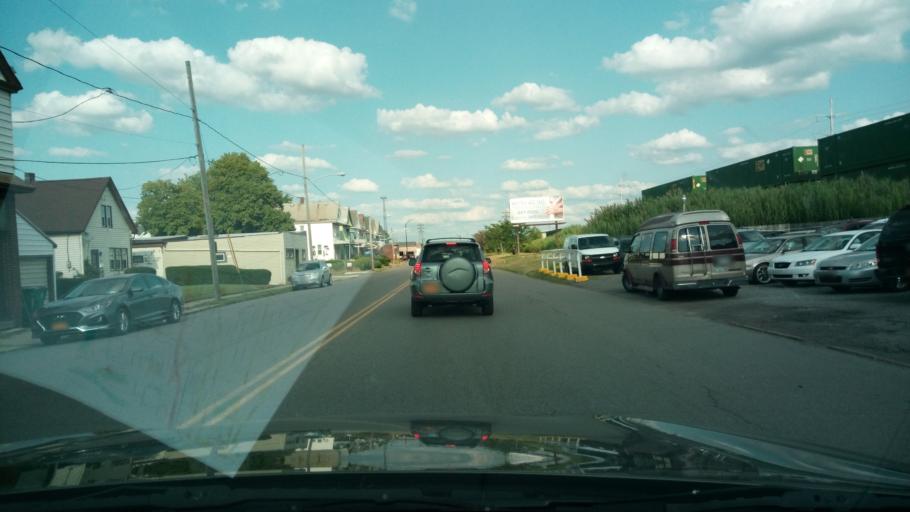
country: US
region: New York
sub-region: Erie County
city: Sloan
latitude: 42.8847
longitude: -78.8061
